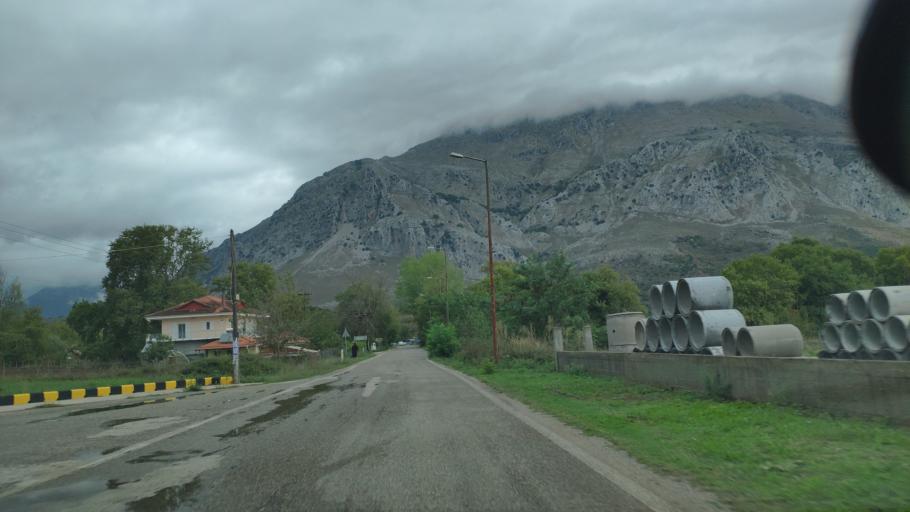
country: GR
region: West Greece
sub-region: Nomos Aitolias kai Akarnanias
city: Krikellos
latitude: 38.9698
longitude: 21.3300
